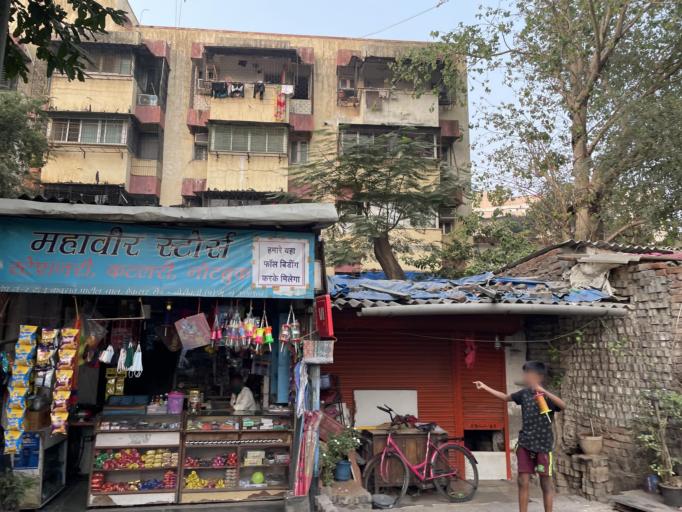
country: IN
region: Maharashtra
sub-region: Mumbai Suburban
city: Borivli
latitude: 19.2399
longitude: 72.8459
